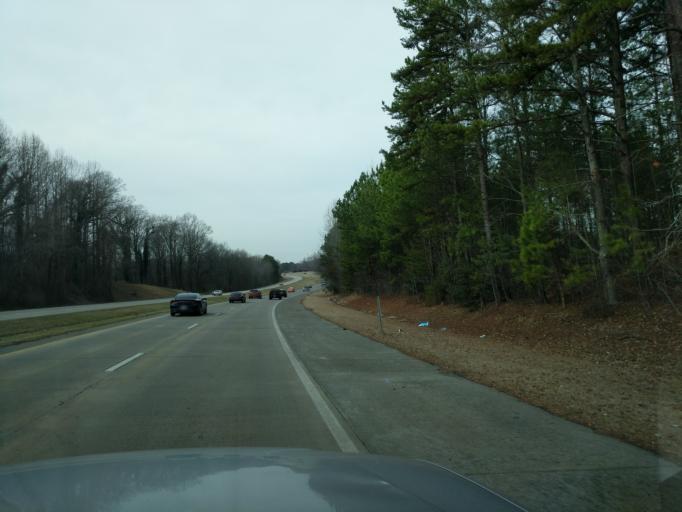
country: US
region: North Carolina
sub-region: Mecklenburg County
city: Charlotte
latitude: 35.1820
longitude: -80.8929
